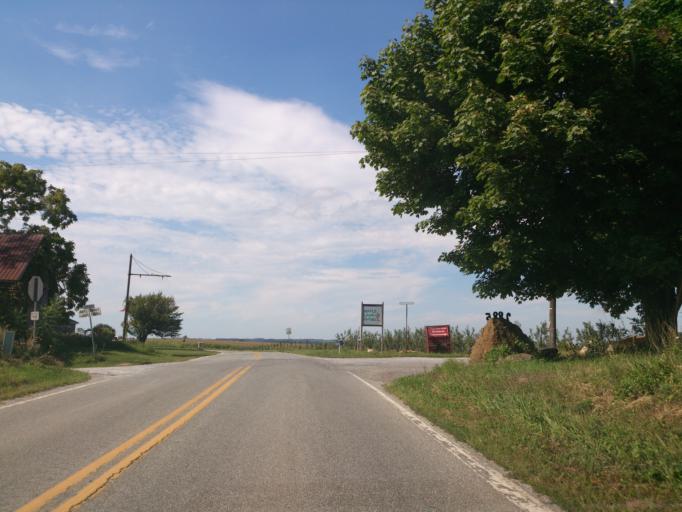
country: US
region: Pennsylvania
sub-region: York County
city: Susquehanna Trails
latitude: 39.7788
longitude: -76.4659
